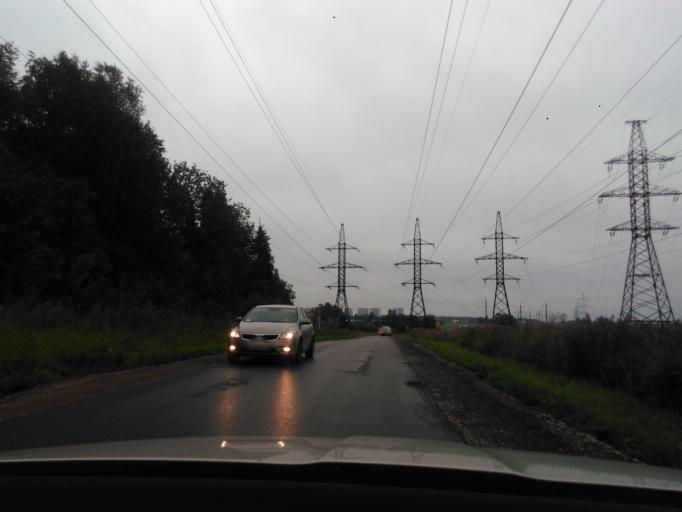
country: RU
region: Moskovskaya
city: Firsanovka
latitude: 55.9494
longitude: 37.2228
